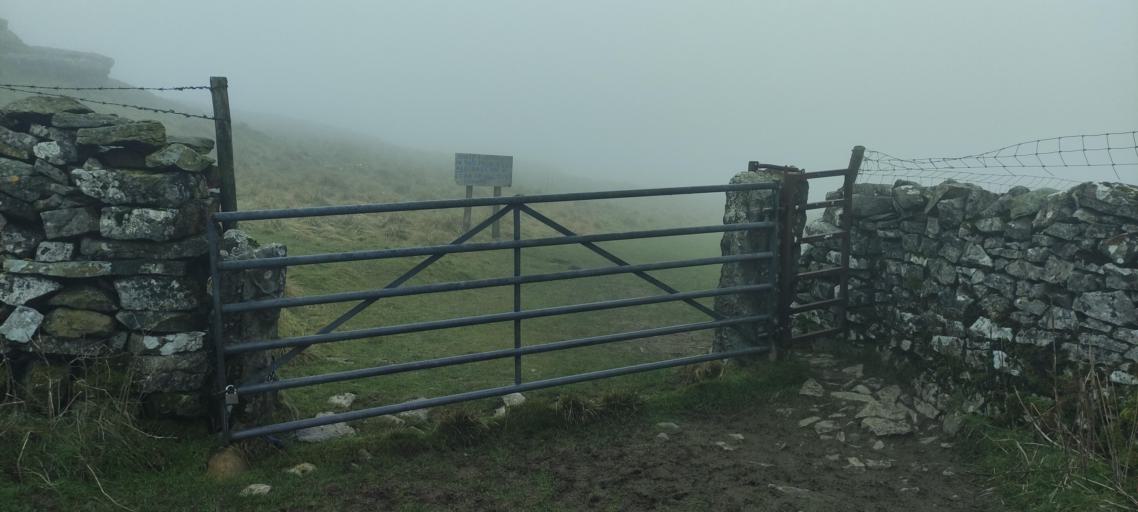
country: GB
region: England
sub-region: North Yorkshire
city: Settle
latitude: 54.0723
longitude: -2.2621
